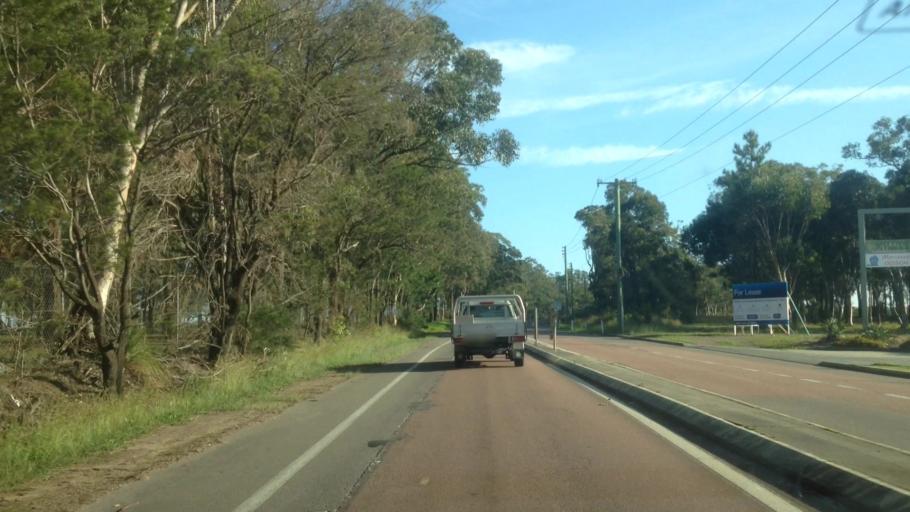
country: AU
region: New South Wales
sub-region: Lake Macquarie Shire
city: Dora Creek
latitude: -33.1164
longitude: 151.4783
